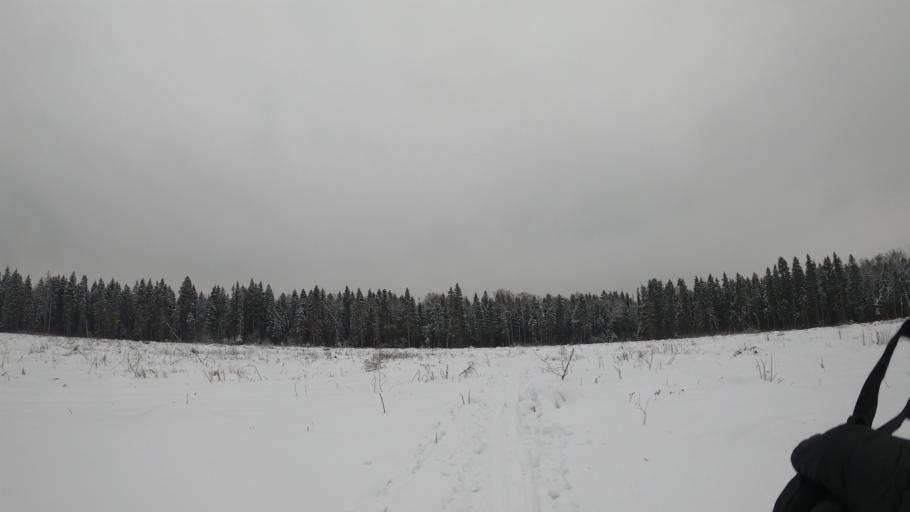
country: RU
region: Moskovskaya
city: Firsanovka
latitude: 55.9623
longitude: 37.2230
